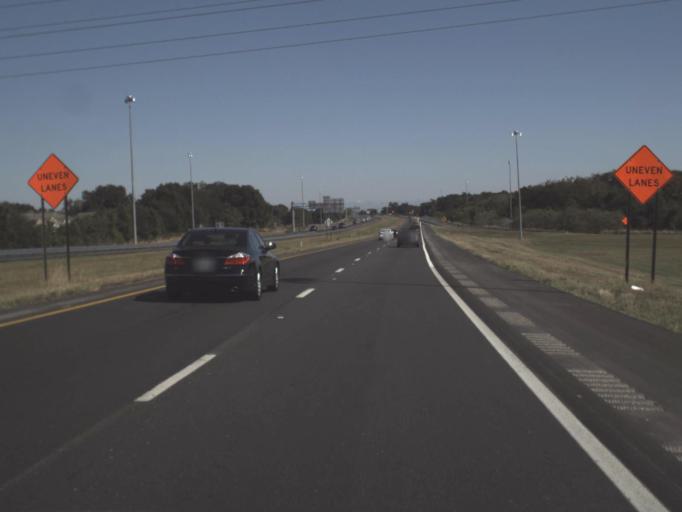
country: US
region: Florida
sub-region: Seminole County
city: Lake Mary
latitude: 28.7985
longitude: -81.3277
